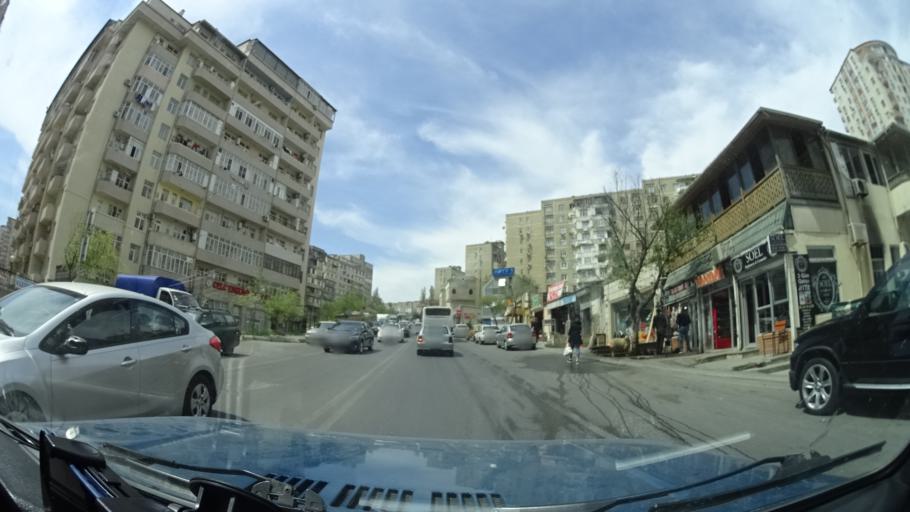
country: AZ
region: Baki
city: Khodzhi-Gasan
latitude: 40.3938
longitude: 49.7939
